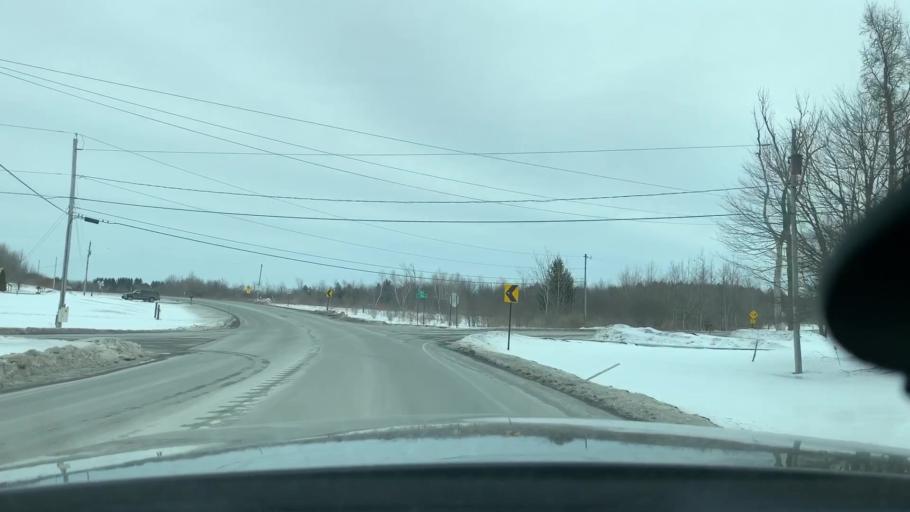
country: US
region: New York
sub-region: Oneida County
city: Utica
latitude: 43.0337
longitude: -75.1847
